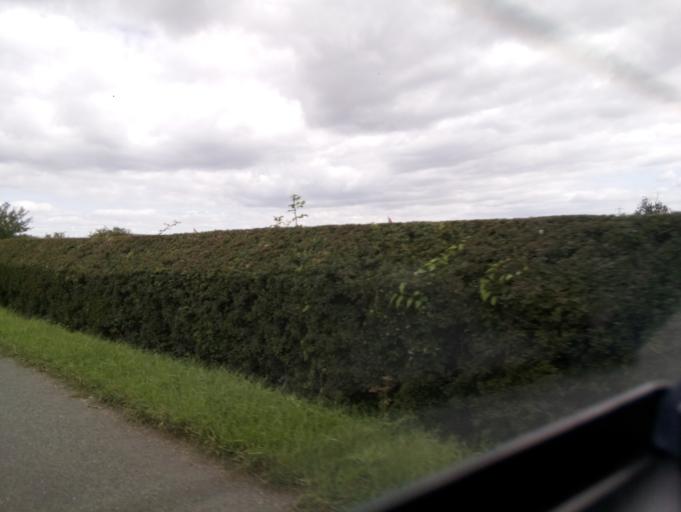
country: GB
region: England
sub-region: Buckinghamshire
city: Newton Longville
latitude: 51.9706
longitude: -0.8181
